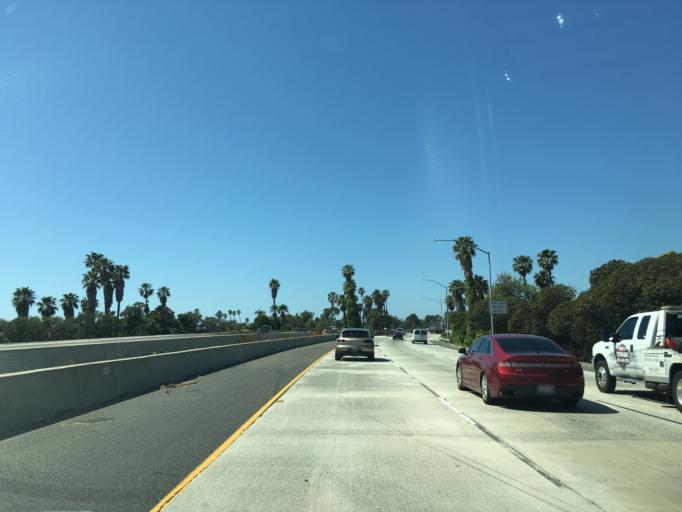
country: US
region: California
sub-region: Ventura County
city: Ventura
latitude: 34.2775
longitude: -119.2993
